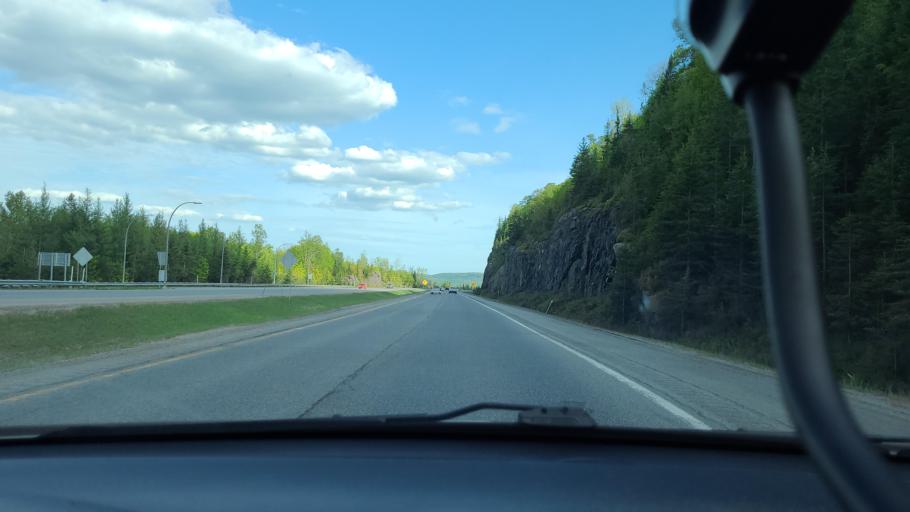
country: CA
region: Quebec
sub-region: Laurentides
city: Sainte-Adele
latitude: 45.9736
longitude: -74.1574
